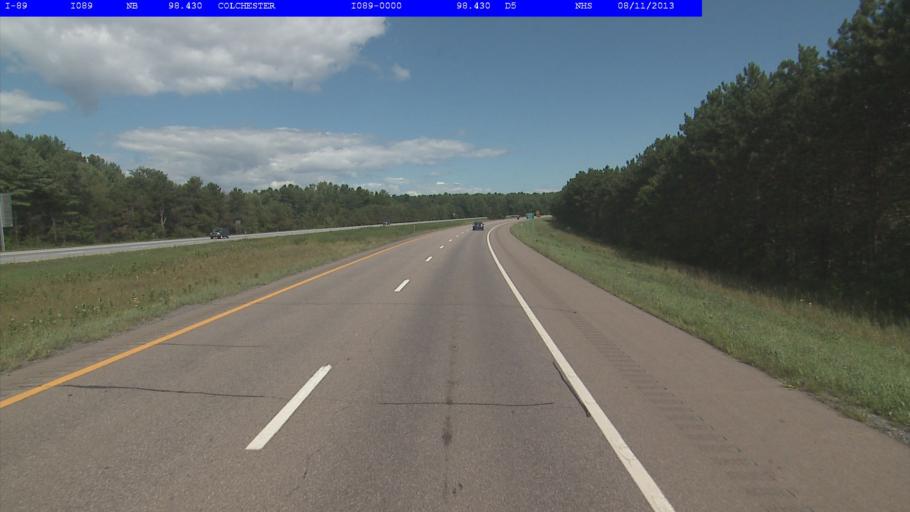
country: US
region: Vermont
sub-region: Chittenden County
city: Colchester
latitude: 44.5975
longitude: -73.1724
